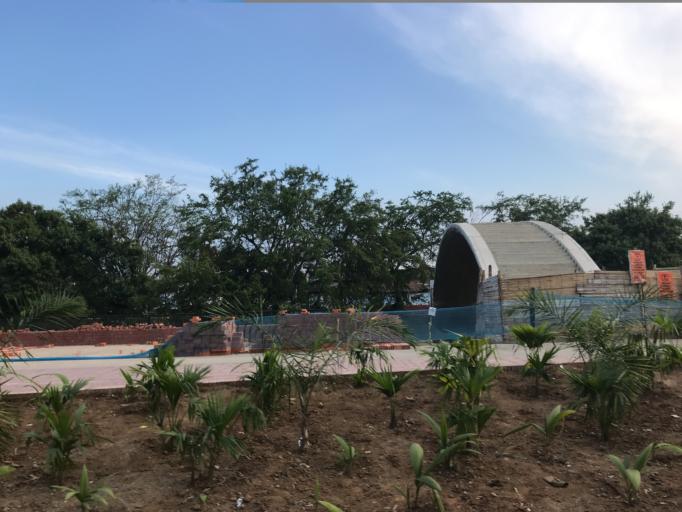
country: CO
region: Valle del Cauca
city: Cali
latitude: 3.4625
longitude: -76.5242
